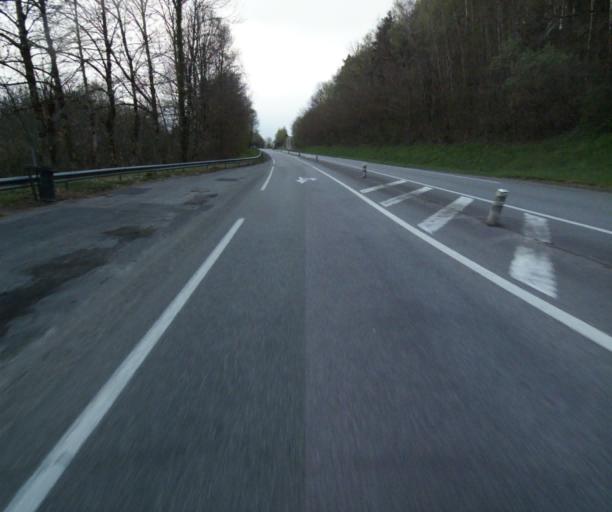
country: FR
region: Limousin
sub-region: Departement de la Correze
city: Naves
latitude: 45.2943
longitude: 1.8078
